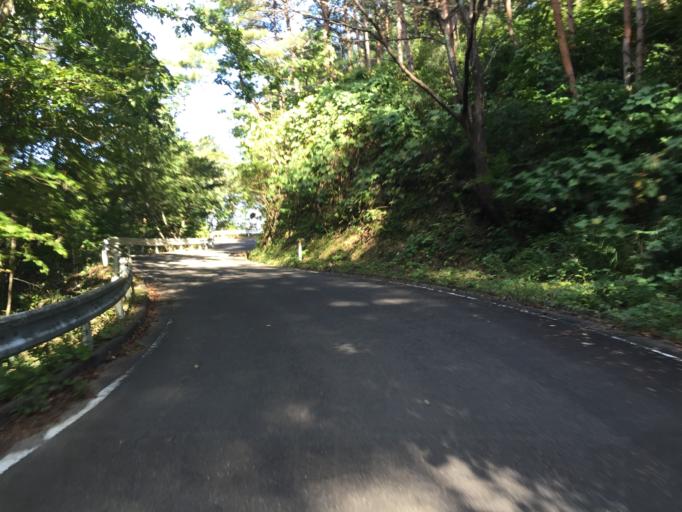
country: JP
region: Fukushima
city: Yanagawamachi-saiwaicho
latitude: 37.8418
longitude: 140.6939
